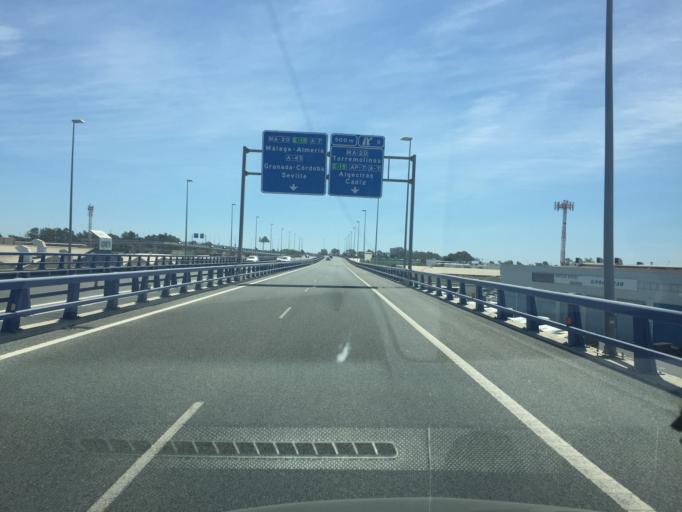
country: ES
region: Andalusia
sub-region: Provincia de Malaga
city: Torremolinos
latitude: 36.6705
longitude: -4.4741
